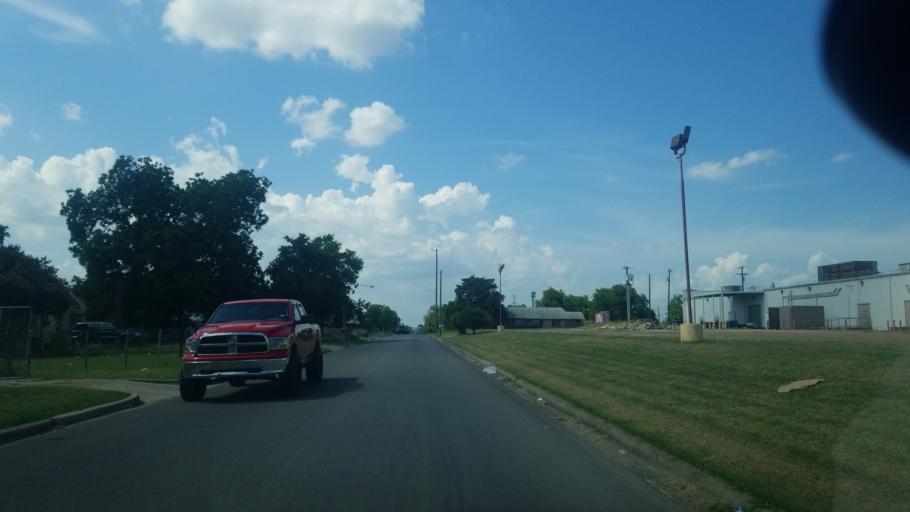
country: US
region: Texas
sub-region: Dallas County
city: Dallas
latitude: 32.7158
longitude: -96.8058
